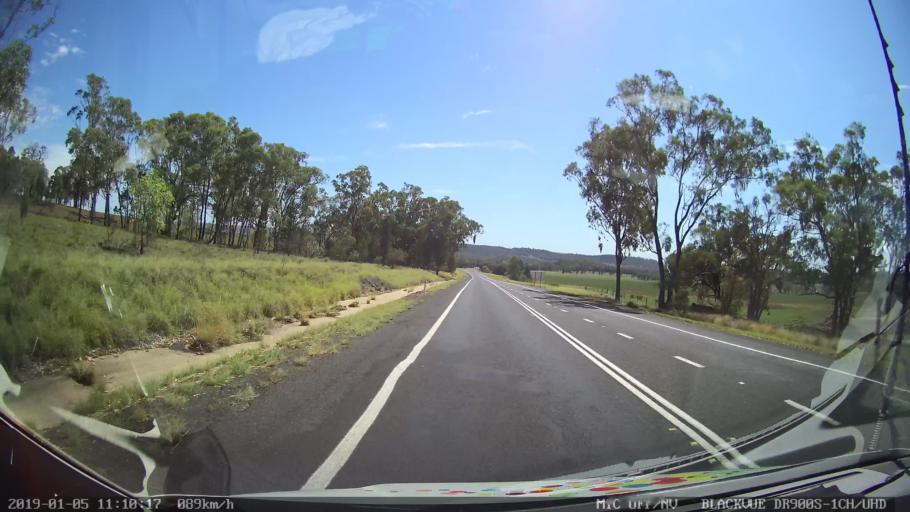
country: AU
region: New South Wales
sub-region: Warrumbungle Shire
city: Coonabarabran
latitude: -31.4081
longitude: 149.2428
